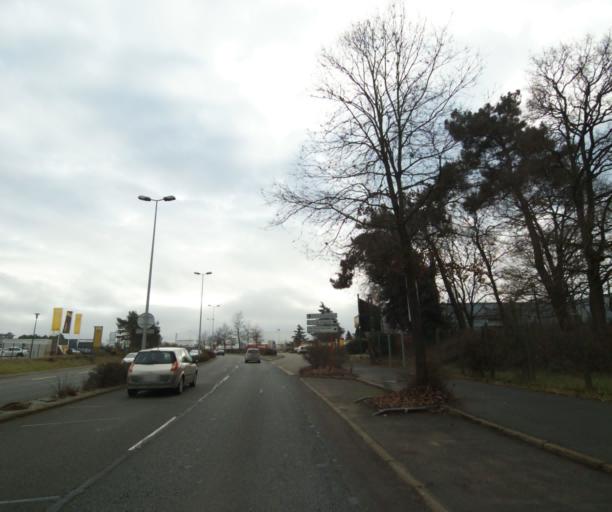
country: FR
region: Pays de la Loire
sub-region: Departement de la Sarthe
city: Le Mans
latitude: 47.9808
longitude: 0.1909
